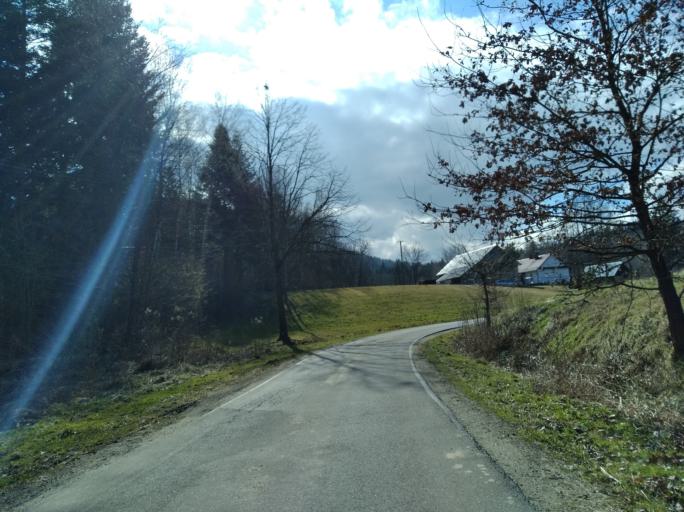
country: PL
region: Subcarpathian Voivodeship
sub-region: Powiat strzyzowski
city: Wysoka Strzyzowska
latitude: 49.8047
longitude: 21.7410
